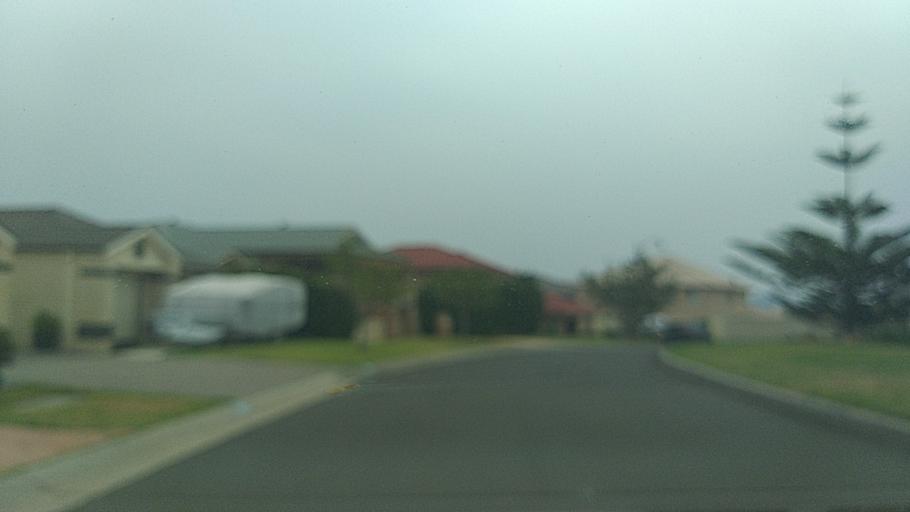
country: AU
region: New South Wales
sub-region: Shellharbour
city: Flinders
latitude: -34.5916
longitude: 150.8518
